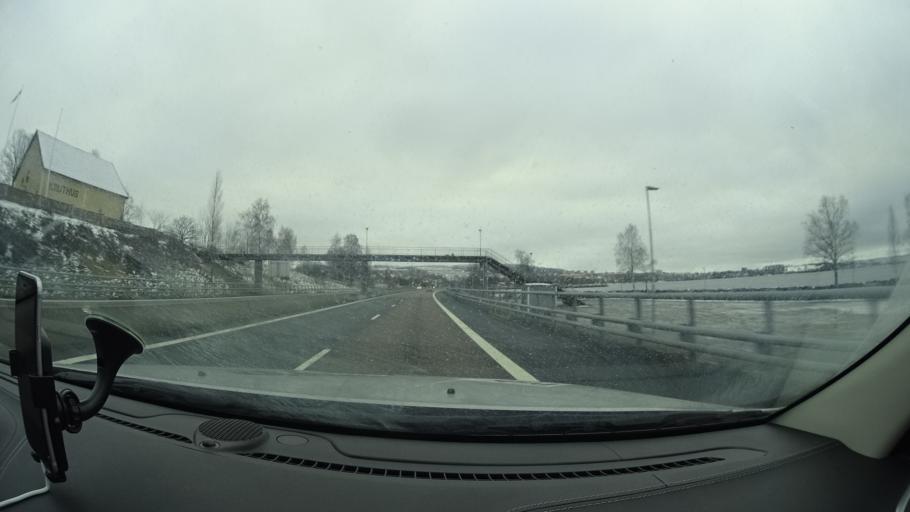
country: SE
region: Joenkoeping
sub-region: Jonkopings Kommun
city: Huskvarna
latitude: 57.8012
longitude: 14.2712
